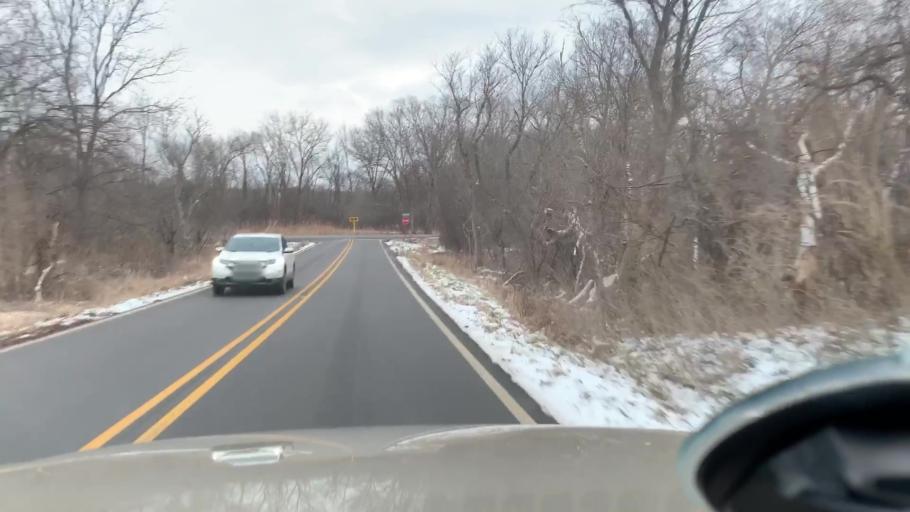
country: US
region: Michigan
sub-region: Jackson County
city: Spring Arbor
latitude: 42.2000
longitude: -84.5221
